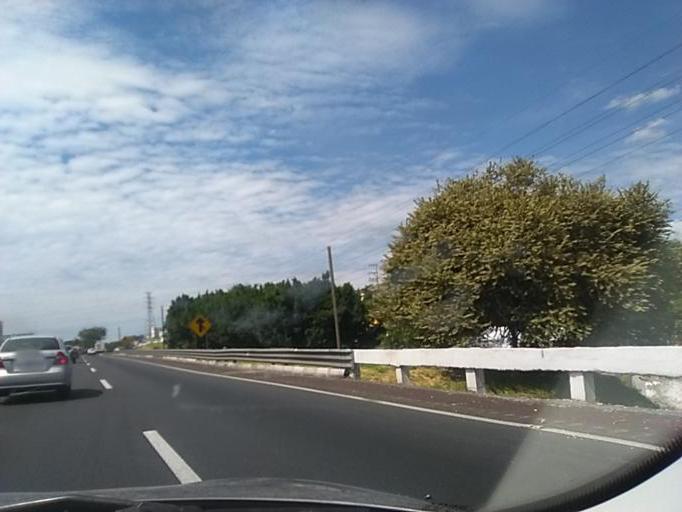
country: MX
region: Morelos
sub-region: Cuernavaca
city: Cuernavaca
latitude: 18.9015
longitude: -99.2194
